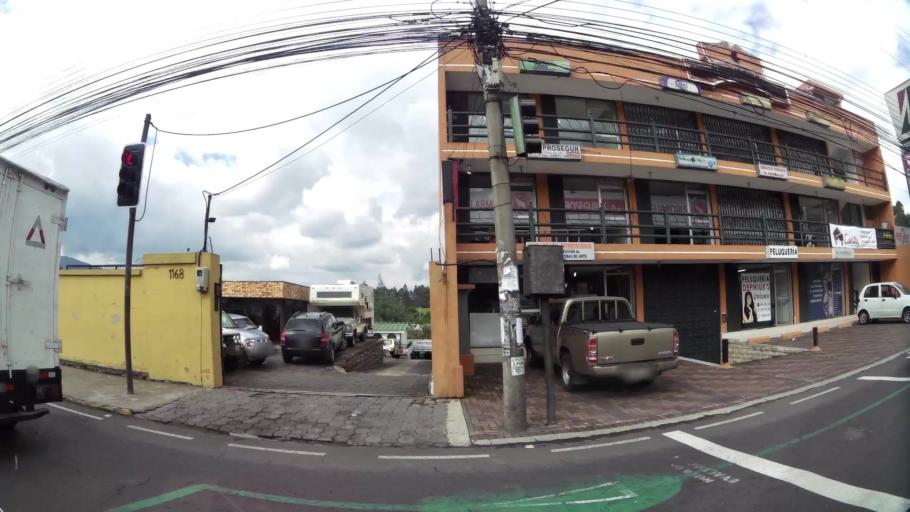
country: EC
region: Pichincha
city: Sangolqui
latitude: -0.3206
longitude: -78.4502
